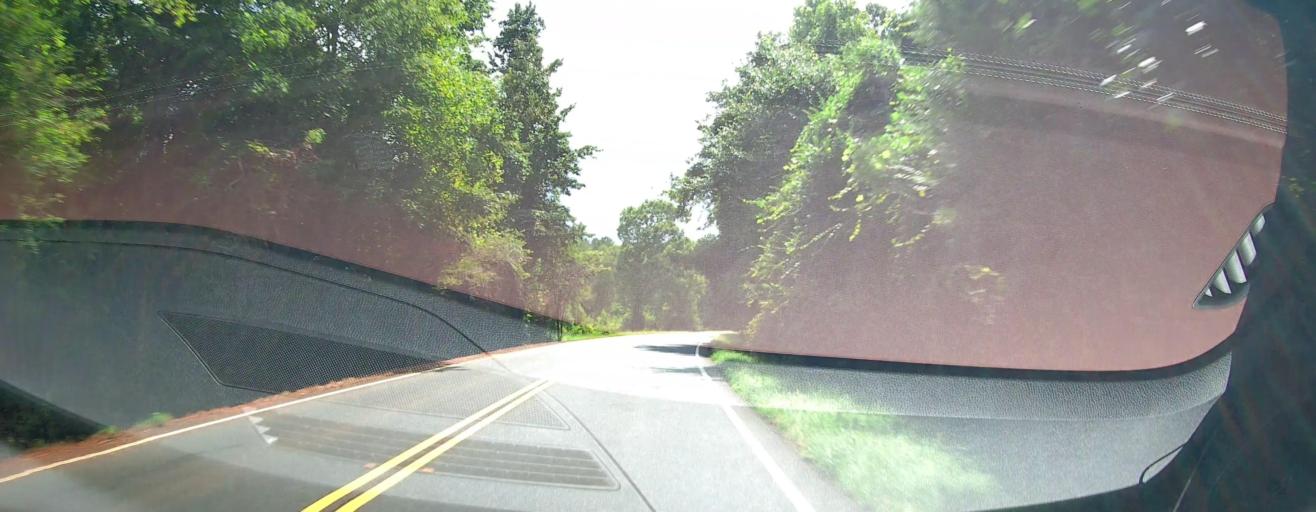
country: US
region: Georgia
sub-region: Crawford County
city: Knoxville
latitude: 32.8764
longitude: -83.9770
